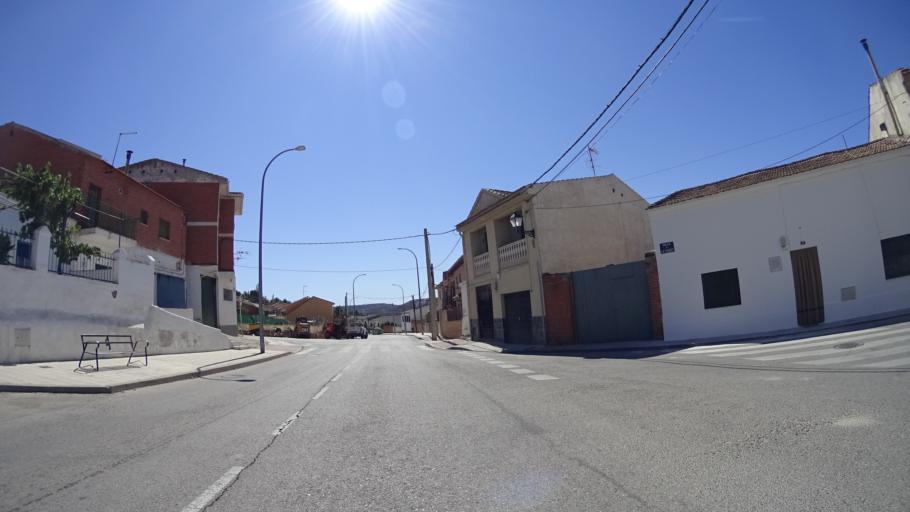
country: ES
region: Madrid
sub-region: Provincia de Madrid
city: Morata de Tajuna
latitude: 40.2323
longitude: -3.4343
